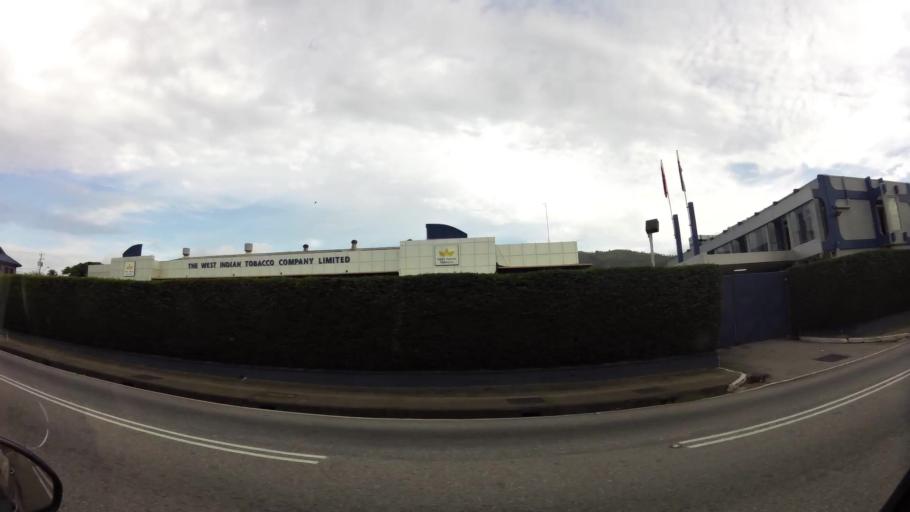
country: TT
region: Tunapuna/Piarco
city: Tunapuna
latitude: 10.6500
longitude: -61.4294
